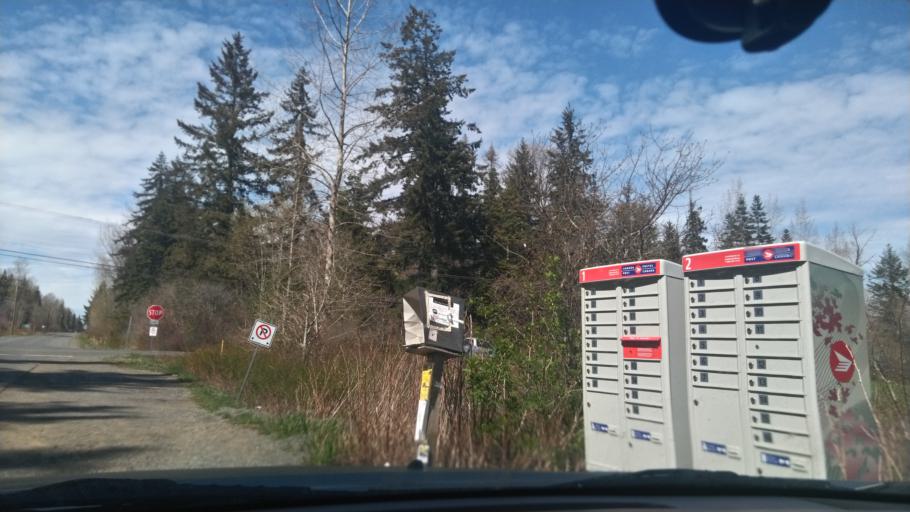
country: CA
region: British Columbia
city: Courtenay
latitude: 49.7059
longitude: -125.0248
